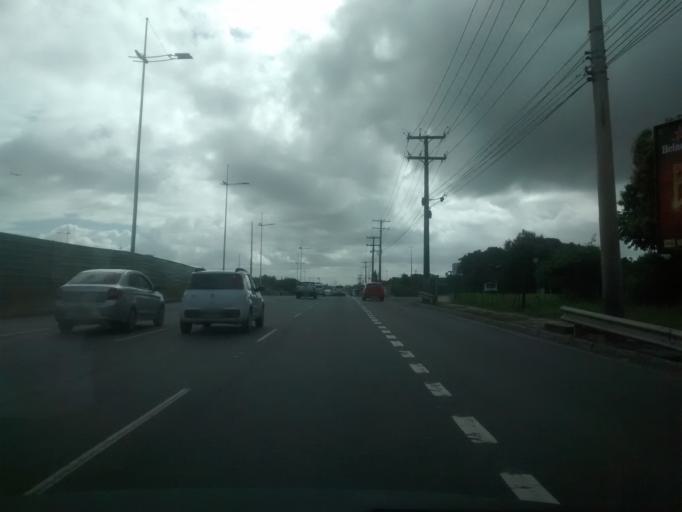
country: BR
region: Bahia
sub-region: Salvador
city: Salvador
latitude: -12.9555
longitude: -38.4284
